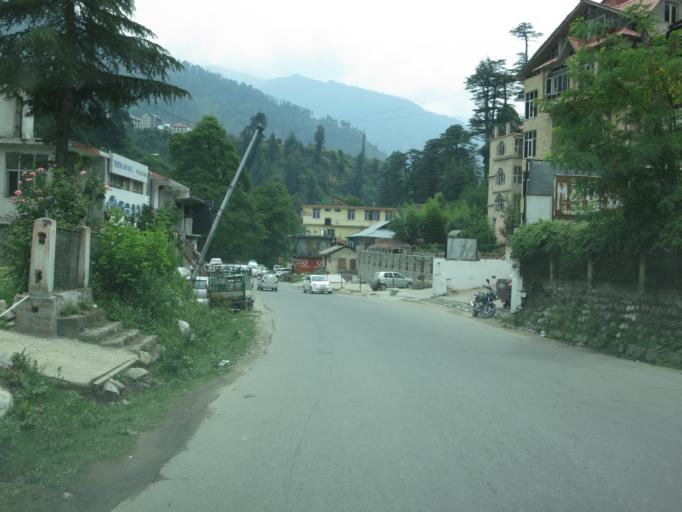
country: IN
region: Himachal Pradesh
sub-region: Kulu
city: Manali
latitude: 32.2220
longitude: 77.1912
